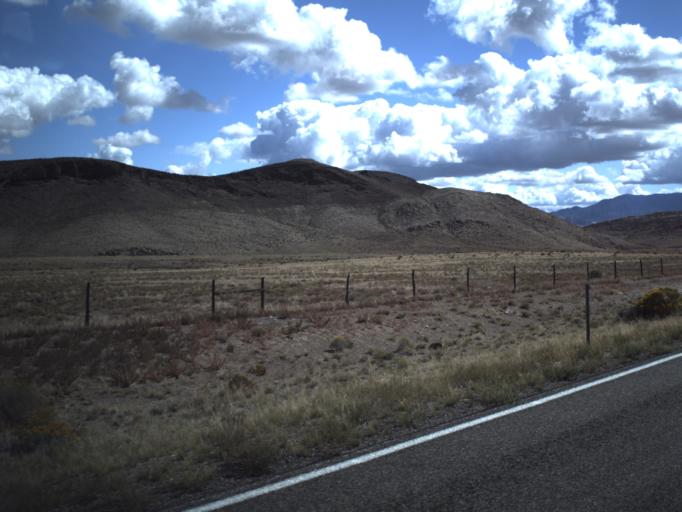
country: US
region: Utah
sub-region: Beaver County
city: Milford
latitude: 38.5946
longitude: -113.8243
